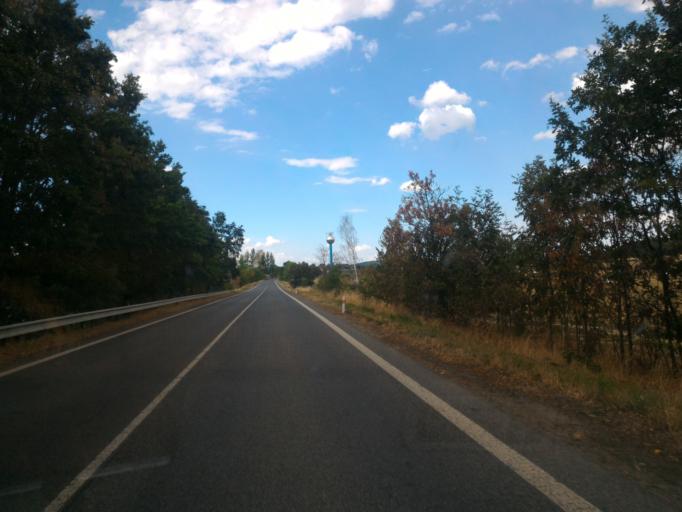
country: CZ
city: Jablonne v Podjestedi
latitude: 50.7474
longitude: 14.7598
